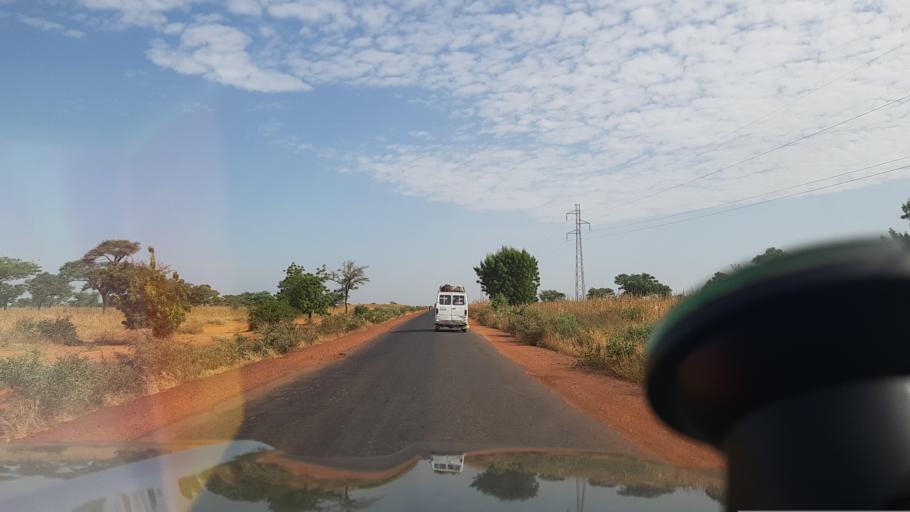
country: ML
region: Segou
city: Segou
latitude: 13.5393
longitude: -6.1225
